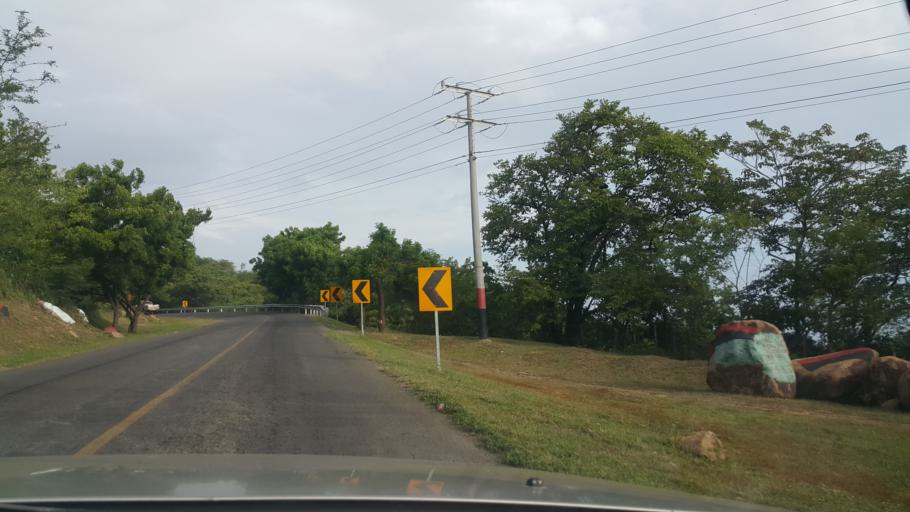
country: NI
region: Managua
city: Masachapa
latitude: 11.8157
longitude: -86.4779
